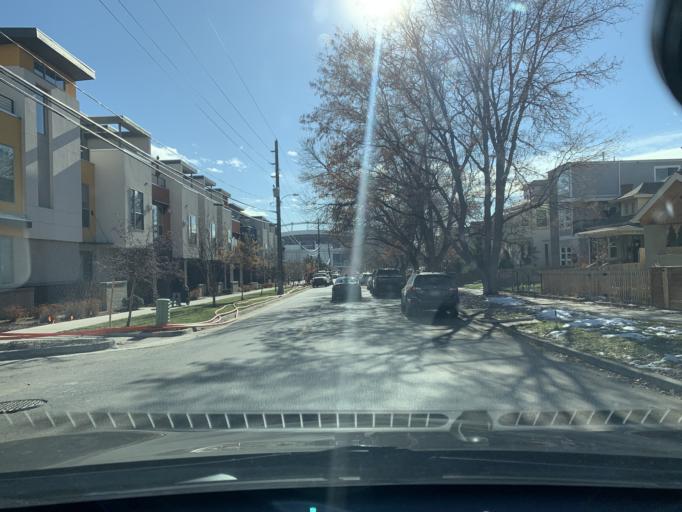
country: US
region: Colorado
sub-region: Denver County
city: Denver
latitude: 39.7498
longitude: -105.0206
